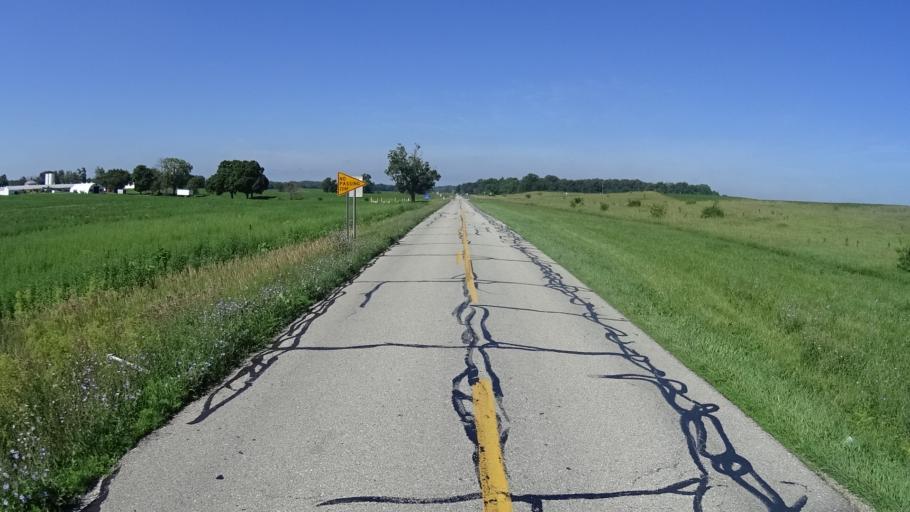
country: US
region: Indiana
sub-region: Madison County
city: Pendleton
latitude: 39.9896
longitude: -85.7688
